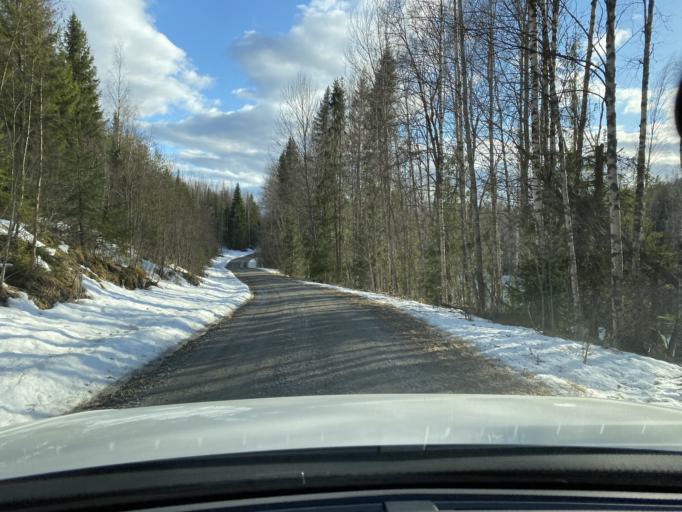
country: FI
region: Pirkanmaa
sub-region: Lounais-Pirkanmaa
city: Mouhijaervi
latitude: 61.4542
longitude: 22.9601
